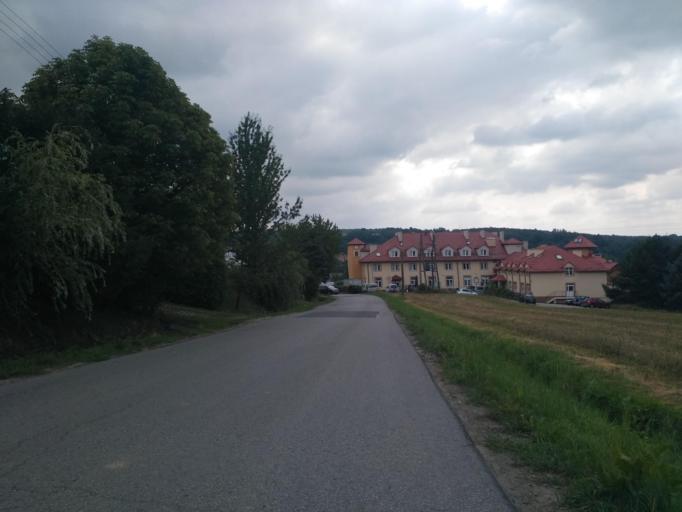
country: PL
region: Subcarpathian Voivodeship
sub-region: Powiat rzeszowski
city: Chmielnik
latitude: 49.9849
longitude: 22.1193
